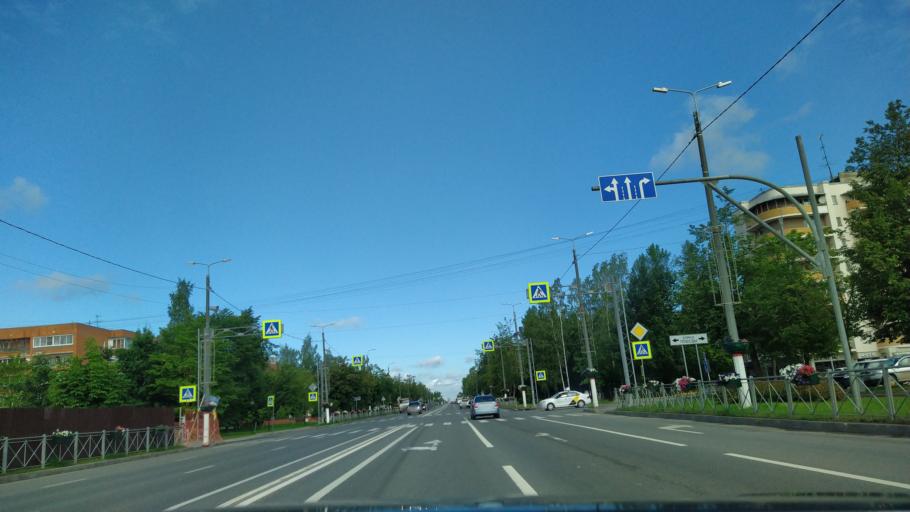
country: RU
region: Leningrad
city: Tosno
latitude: 59.5419
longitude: 30.8760
